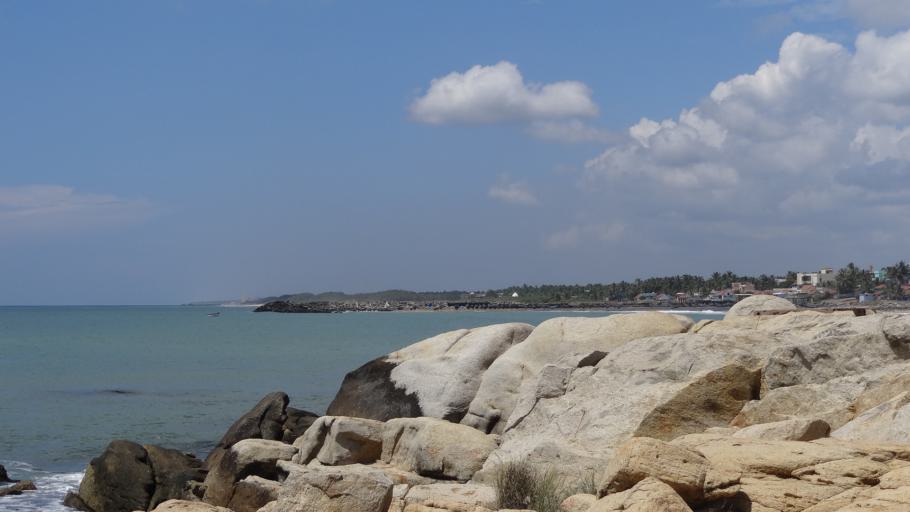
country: IN
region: Tamil Nadu
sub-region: Kanniyakumari
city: Kanniyakumari
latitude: 8.0784
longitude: 77.5316
